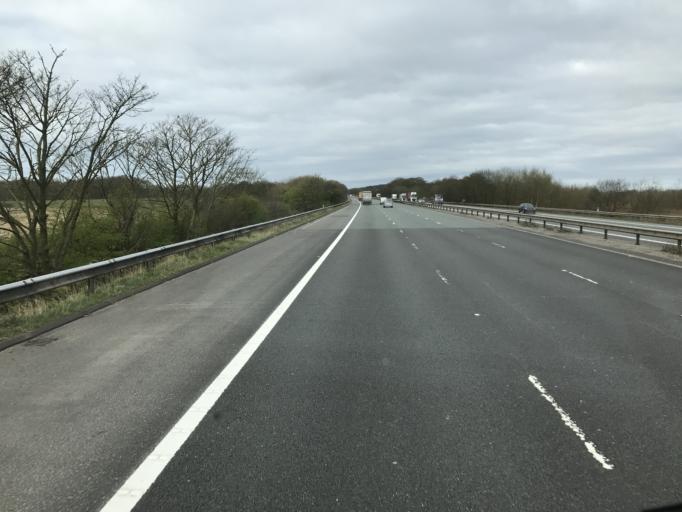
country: GB
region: England
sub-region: Warrington
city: Burtonwood
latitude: 53.4120
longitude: -2.6922
